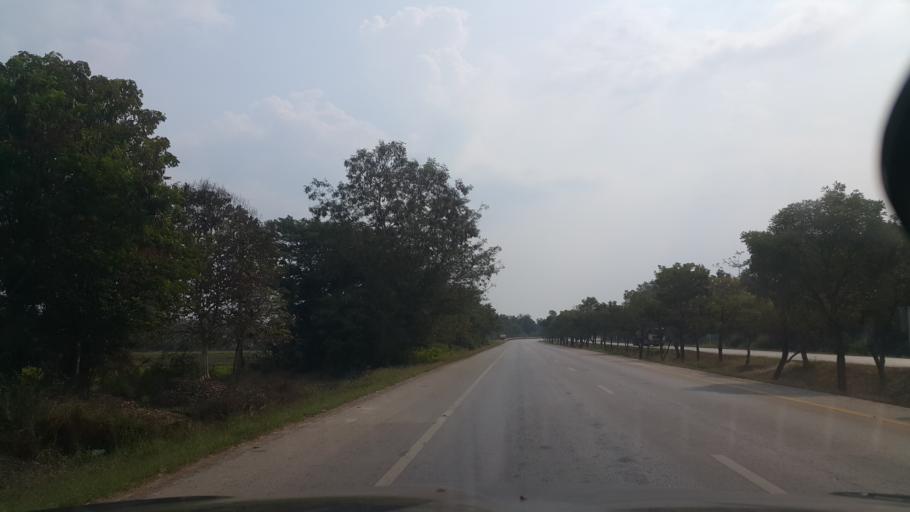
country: TH
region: Sukhothai
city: Sukhothai
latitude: 17.0598
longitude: 99.8943
